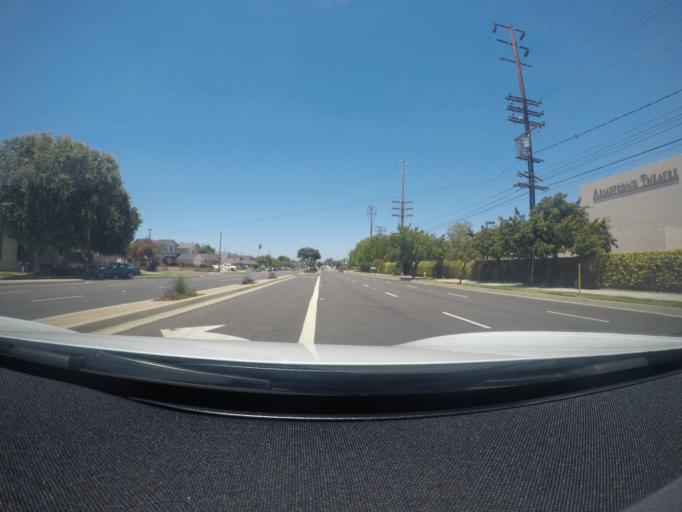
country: US
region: California
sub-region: Los Angeles County
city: Torrance
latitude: 33.8392
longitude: -118.3448
